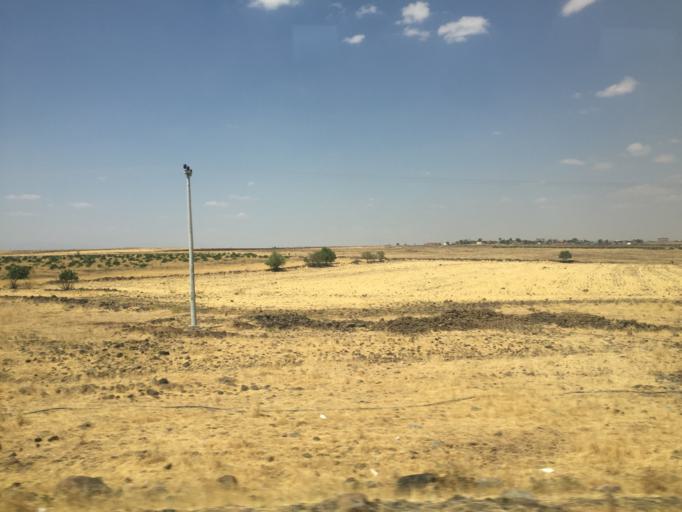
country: TR
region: Sanliurfa
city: Siverek
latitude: 37.7726
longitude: 39.4461
